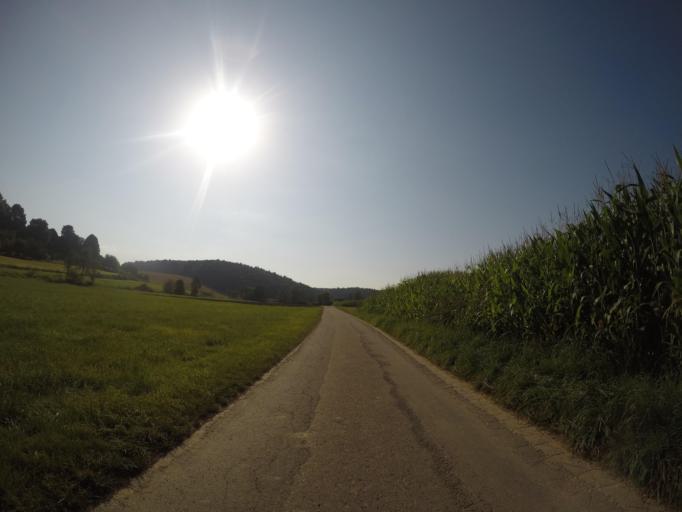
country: DE
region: Baden-Wuerttemberg
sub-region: Tuebingen Region
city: Schnurpflingen
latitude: 48.2603
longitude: 10.0033
